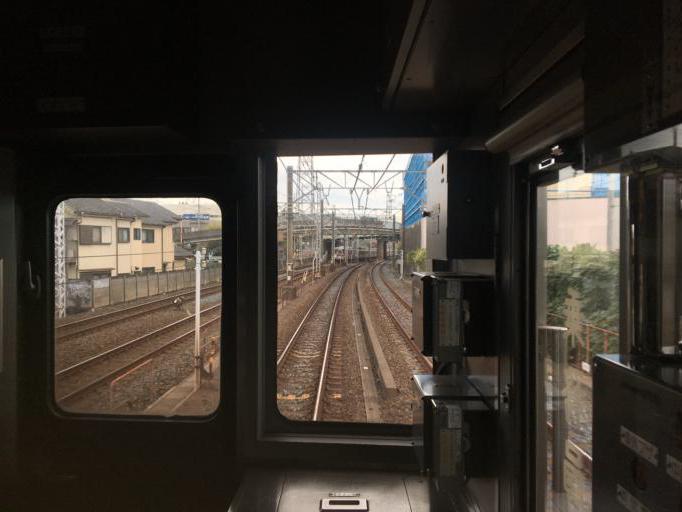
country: JP
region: Saitama
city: Wako
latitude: 35.7849
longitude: 139.6215
